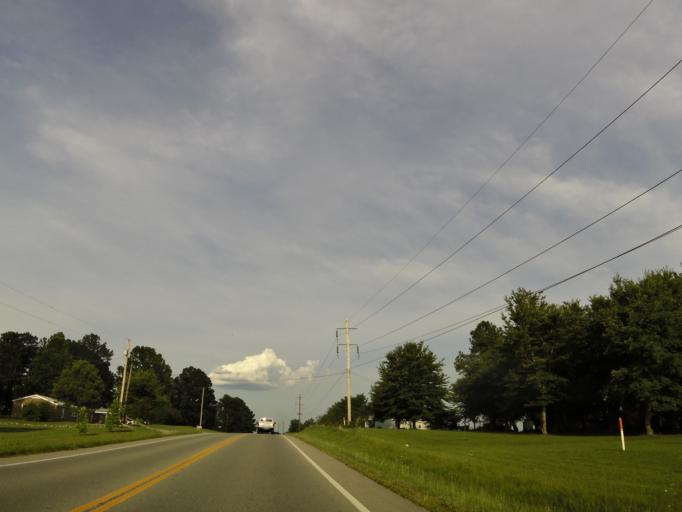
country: US
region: Tennessee
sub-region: Humphreys County
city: McEwen
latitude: 36.0928
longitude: -87.5329
